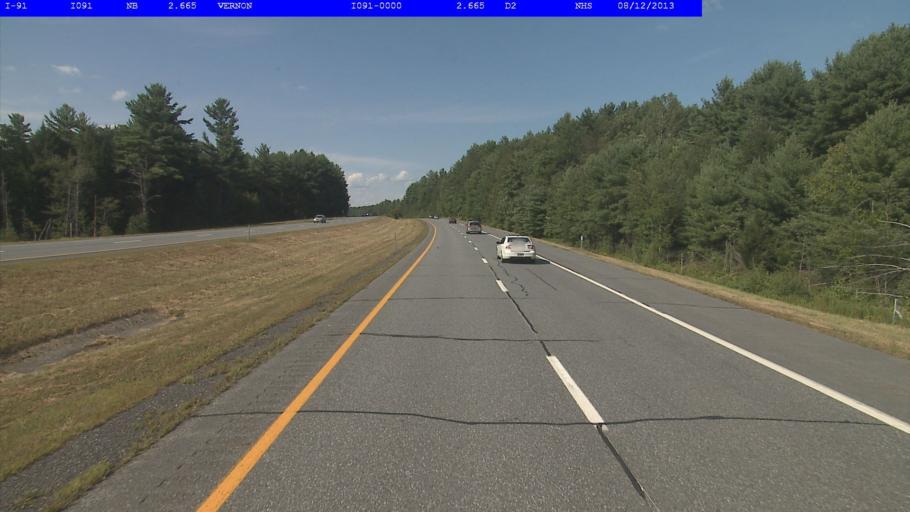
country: US
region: New Hampshire
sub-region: Cheshire County
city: Hinsdale
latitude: 42.7681
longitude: -72.5624
